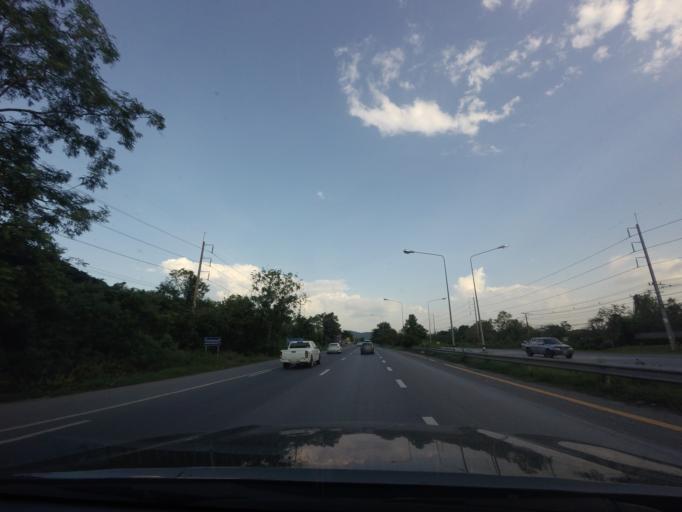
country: TH
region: Sara Buri
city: Saraburi
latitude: 14.5100
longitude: 100.9048
